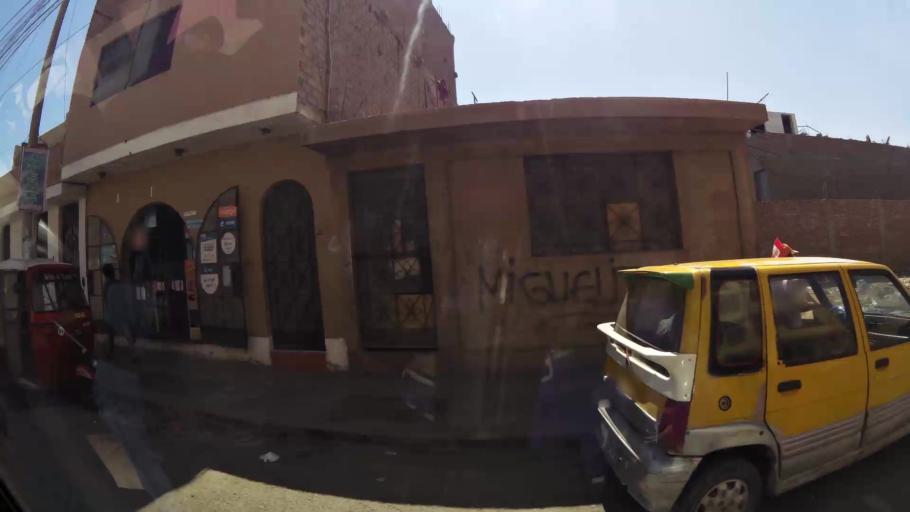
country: PE
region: Ica
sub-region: Provincia de Ica
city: Ica
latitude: -14.0658
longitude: -75.7258
